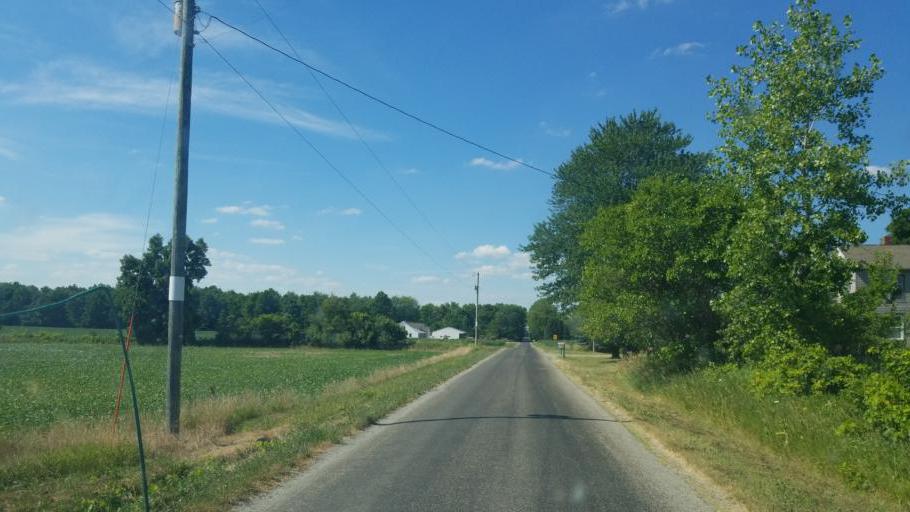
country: US
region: Ohio
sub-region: Williams County
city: Edgerton
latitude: 41.3745
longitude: -84.7863
